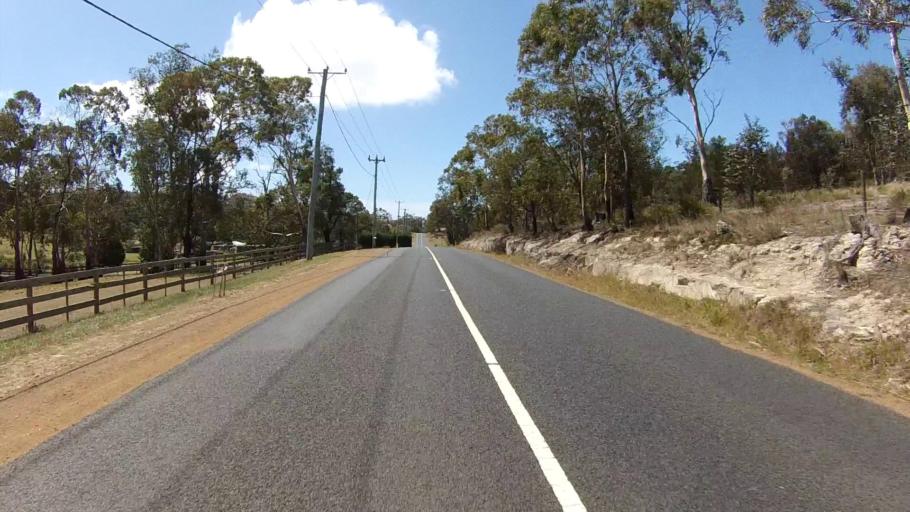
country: AU
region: Tasmania
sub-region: Clarence
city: Sandford
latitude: -42.9618
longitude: 147.4741
